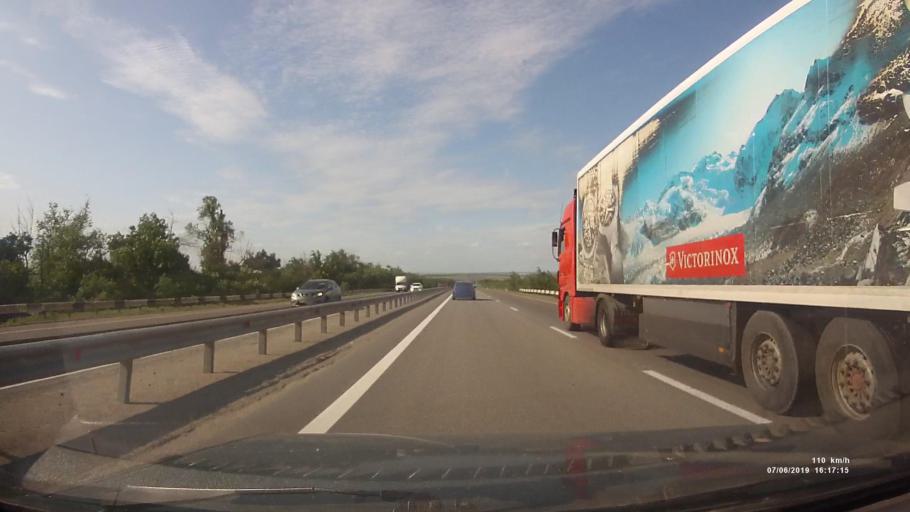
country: RU
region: Rostov
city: Likhoy
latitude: 48.1958
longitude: 40.2667
